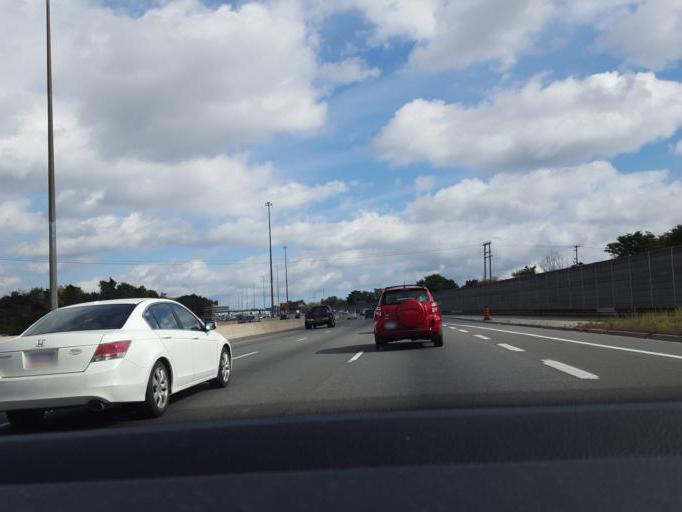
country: CA
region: Ontario
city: Scarborough
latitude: 43.7681
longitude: -79.3163
